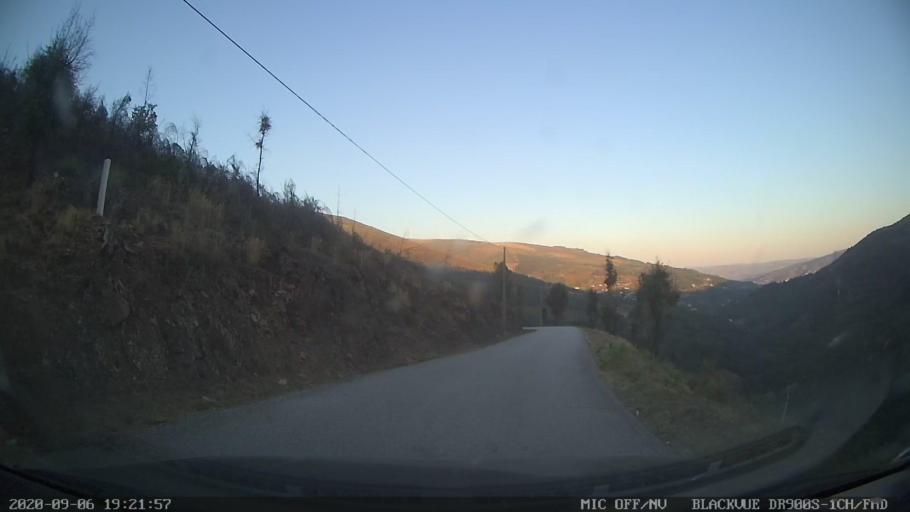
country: PT
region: Vila Real
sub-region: Mesao Frio
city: Mesao Frio
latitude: 41.1838
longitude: -7.9284
